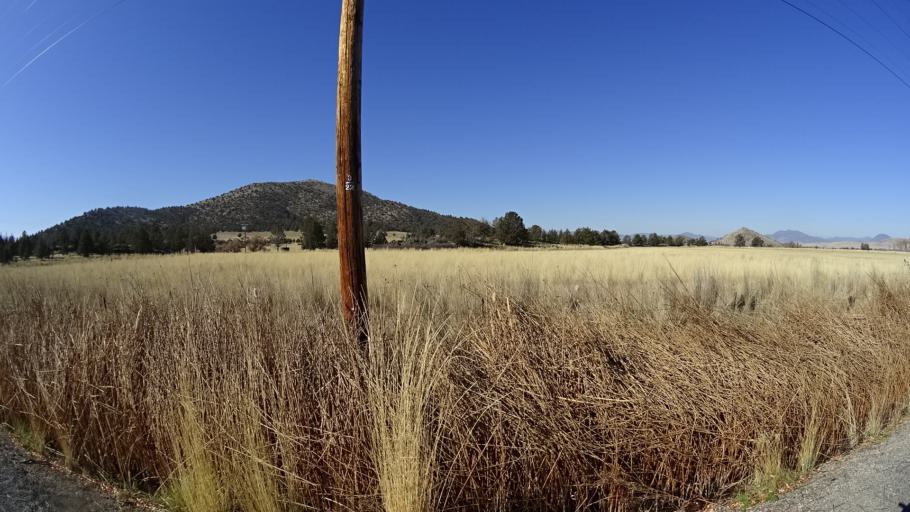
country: US
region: California
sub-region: Siskiyou County
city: Montague
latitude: 41.6749
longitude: -122.3691
